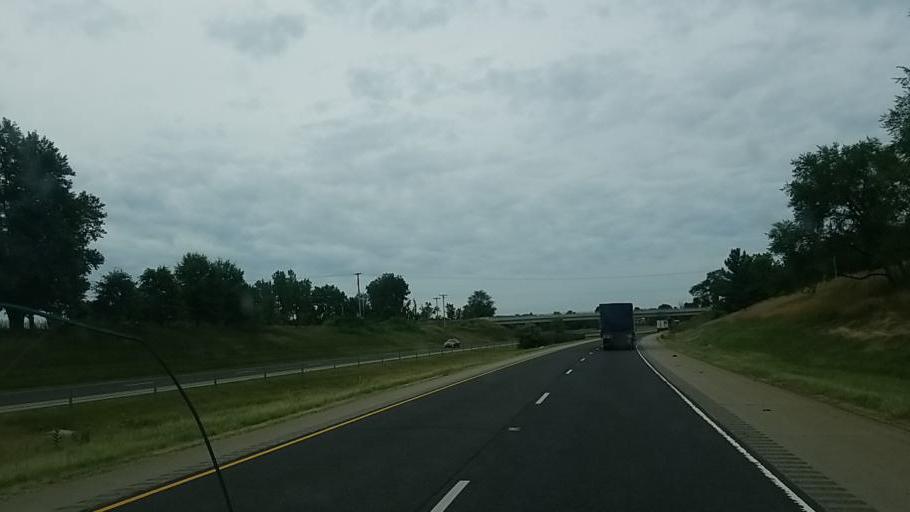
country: US
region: Indiana
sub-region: Steuben County
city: Angola
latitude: 41.6731
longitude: -85.0082
